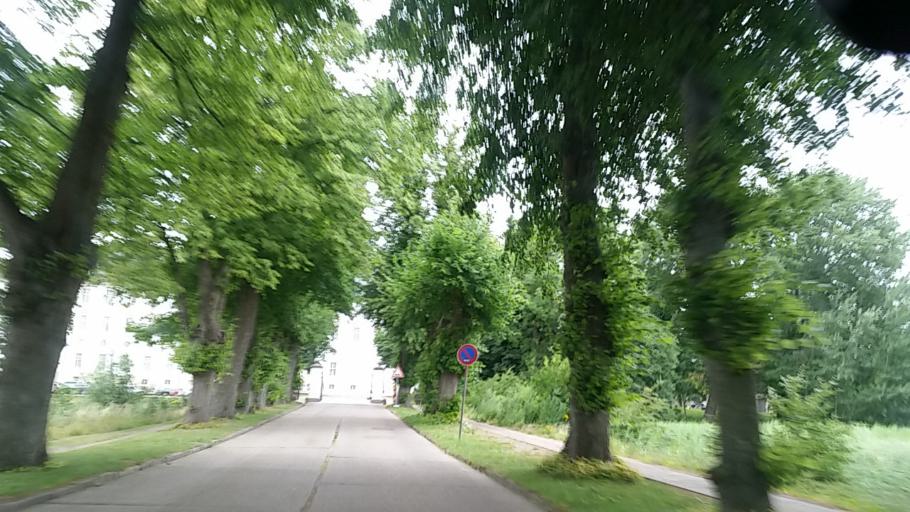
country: DE
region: Schleswig-Holstein
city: Busdorf
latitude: 54.5102
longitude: 9.5417
